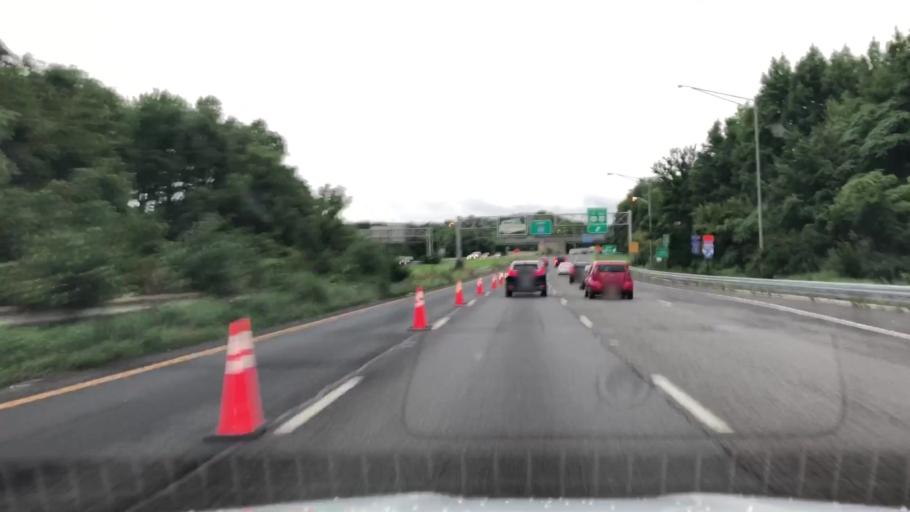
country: US
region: New Jersey
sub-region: Salem County
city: Carneys Point
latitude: 39.6805
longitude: -75.4831
